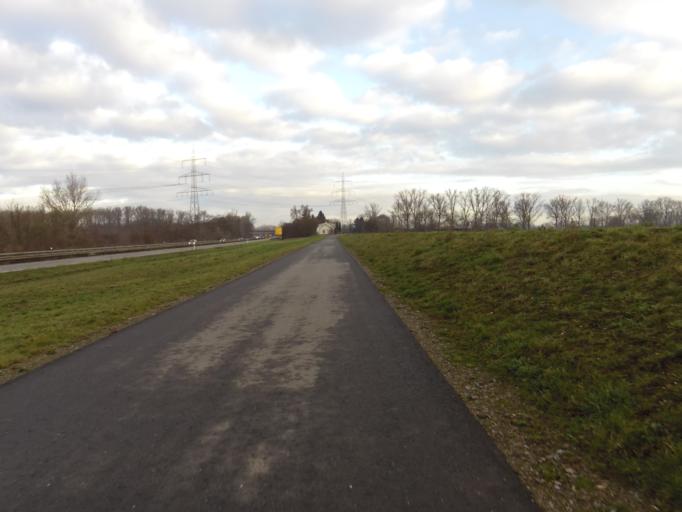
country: DE
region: Rheinland-Pfalz
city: Bobenheim-Roxheim
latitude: 49.5892
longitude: 8.4054
